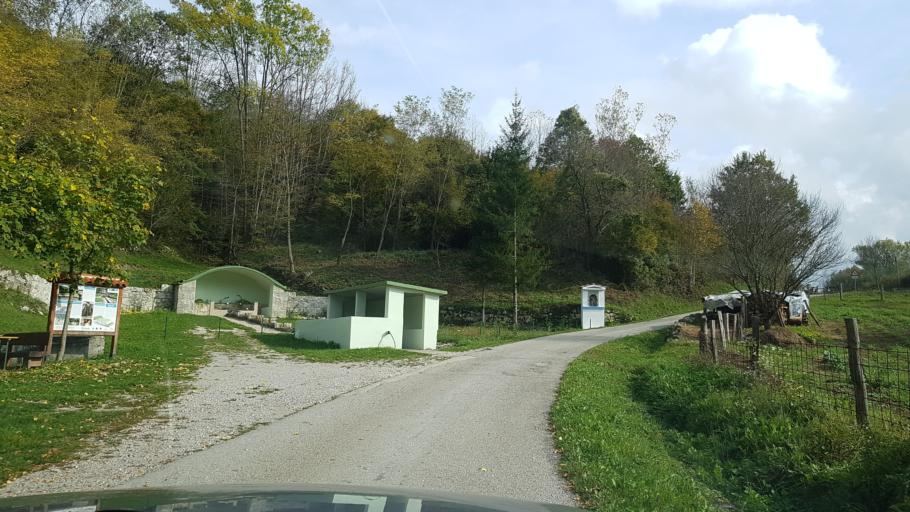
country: HR
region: Istarska
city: Buzet
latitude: 45.4236
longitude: 14.0764
